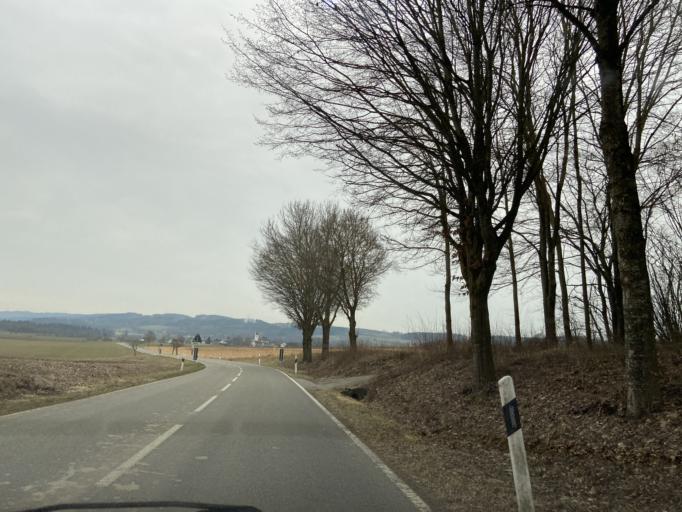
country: DE
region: Baden-Wuerttemberg
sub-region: Tuebingen Region
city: Ostrach
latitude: 47.9255
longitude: 9.3525
